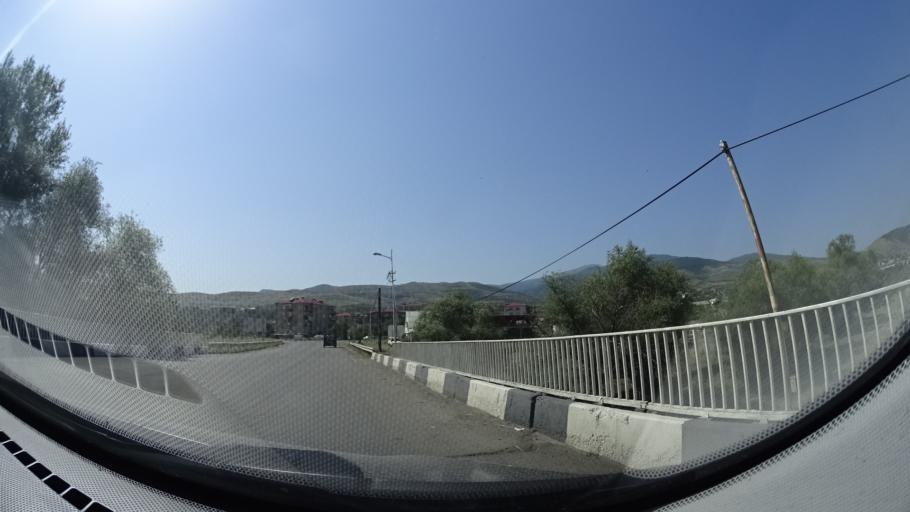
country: GE
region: Samtskhe-Javakheti
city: Akhaltsikhe
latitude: 41.6456
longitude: 43.0015
